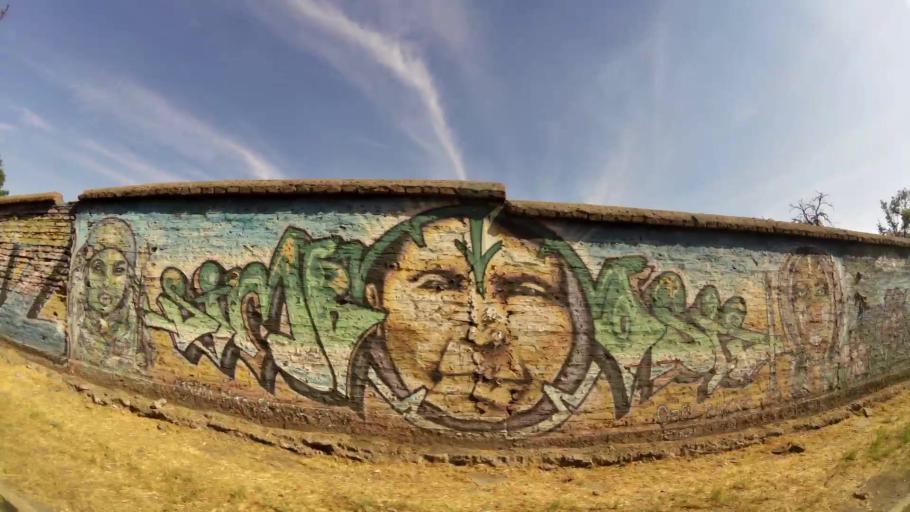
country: CL
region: Santiago Metropolitan
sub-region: Provincia de Santiago
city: Villa Presidente Frei, Nunoa, Santiago, Chile
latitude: -33.4844
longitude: -70.5640
